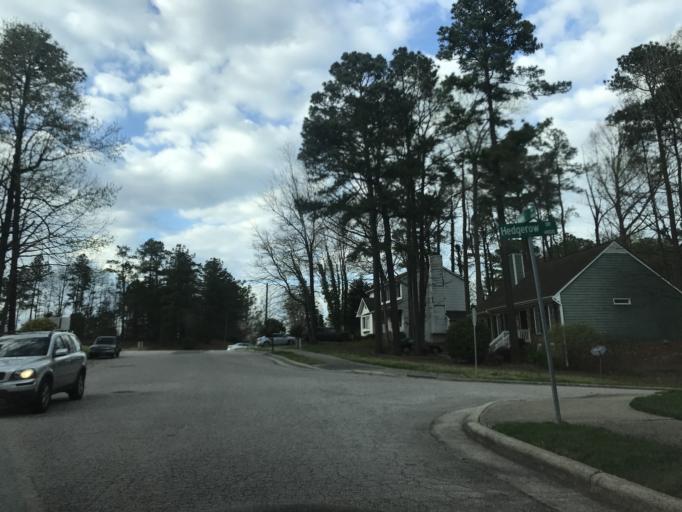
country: US
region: North Carolina
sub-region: Wake County
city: Knightdale
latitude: 35.8668
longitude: -78.5626
